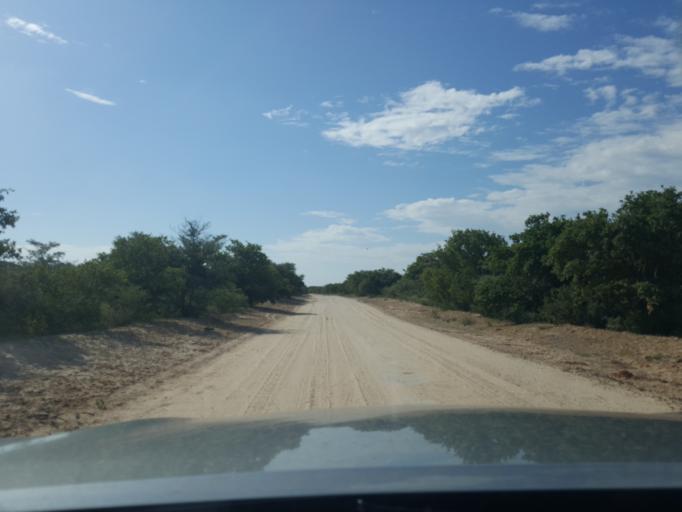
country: BW
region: Kweneng
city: Khudumelapye
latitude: -23.4937
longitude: 24.7012
